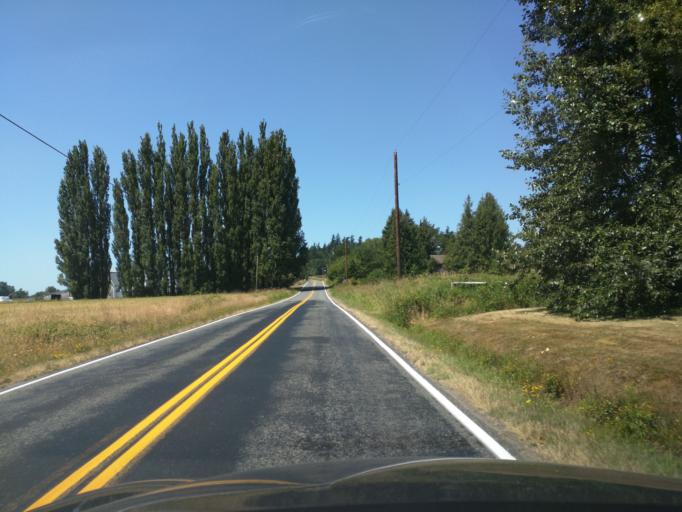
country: US
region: Washington
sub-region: Whatcom County
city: Lynden
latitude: 48.9648
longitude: -122.5600
